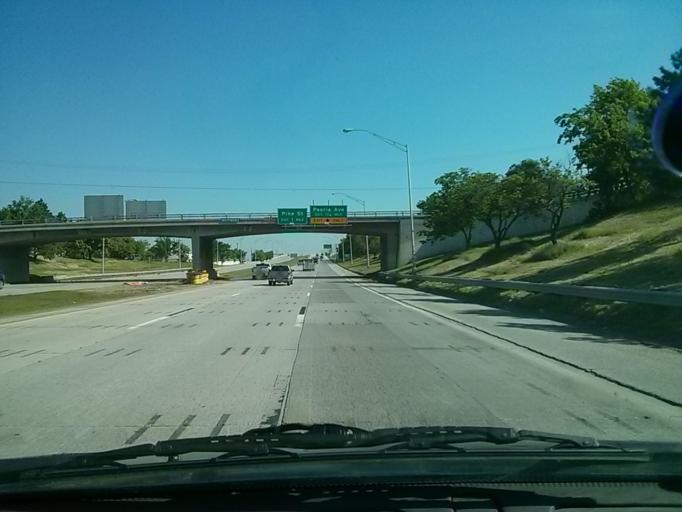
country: US
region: Oklahoma
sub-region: Tulsa County
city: Tulsa
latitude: 36.1654
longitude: -95.9804
